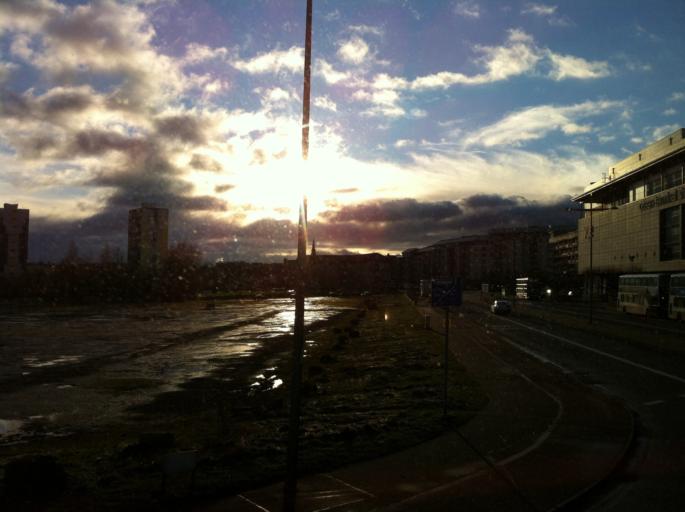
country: GB
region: Scotland
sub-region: West Lothian
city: Seafield
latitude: 55.9811
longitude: -3.1757
